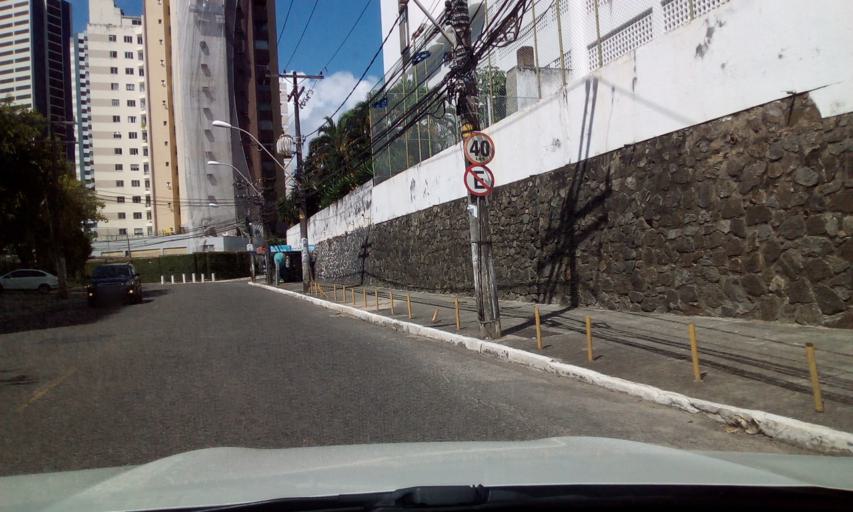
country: BR
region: Bahia
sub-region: Salvador
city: Salvador
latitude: -12.9911
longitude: -38.4666
